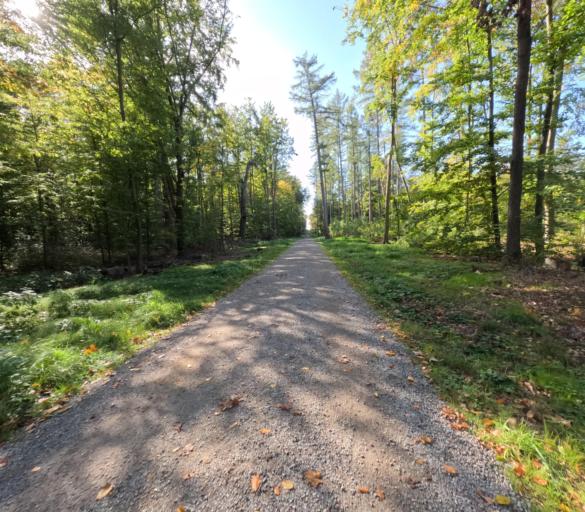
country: DE
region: Saxony
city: Moritzburg
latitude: 51.1736
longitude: 13.6839
